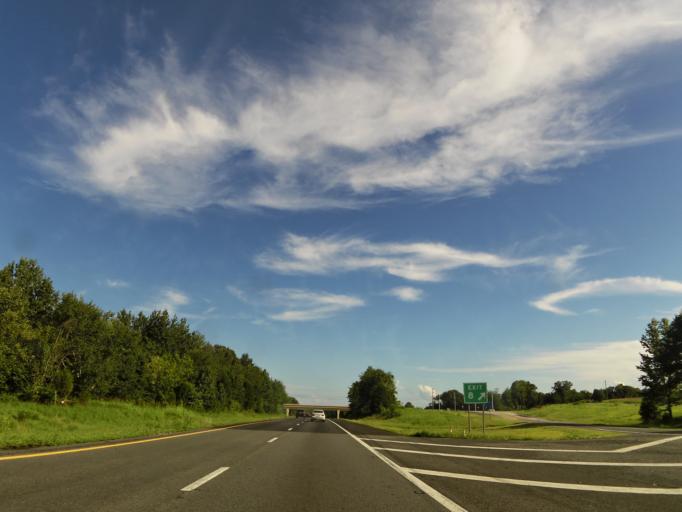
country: US
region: Tennessee
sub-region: Montgomery County
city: Clarksville
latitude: 36.5587
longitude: -87.2515
